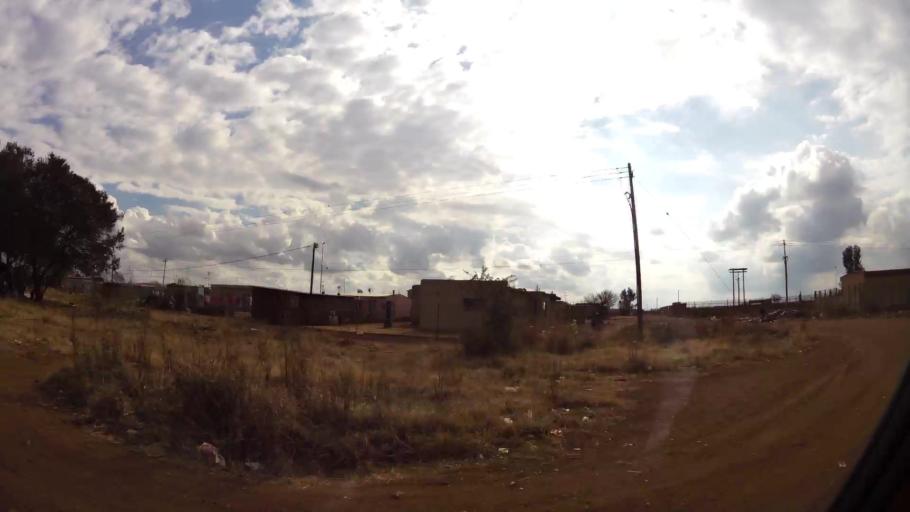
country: ZA
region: Gauteng
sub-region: Sedibeng District Municipality
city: Vanderbijlpark
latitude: -26.7009
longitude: 27.7922
